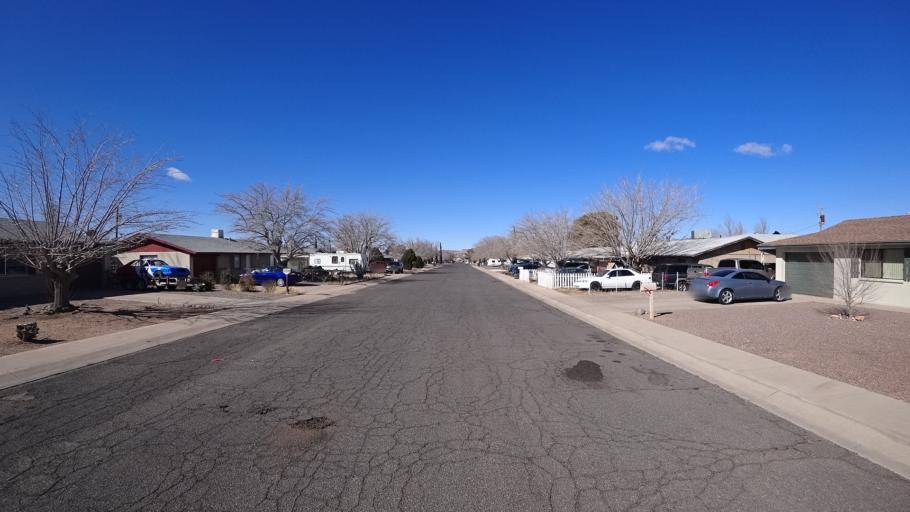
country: US
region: Arizona
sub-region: Mohave County
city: Kingman
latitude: 35.1949
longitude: -114.0160
